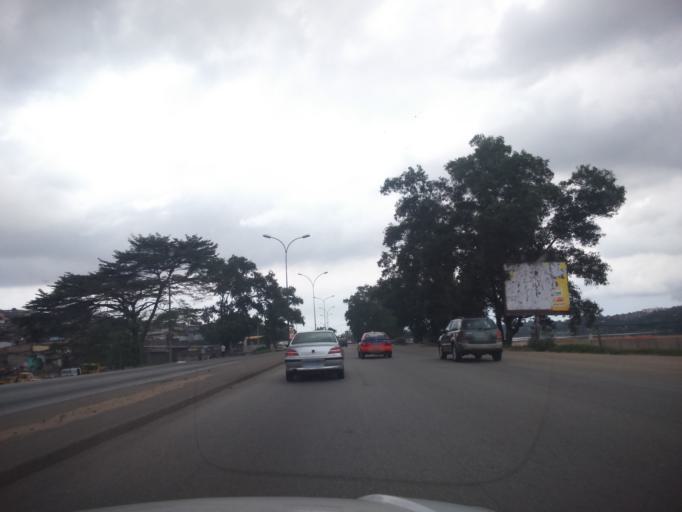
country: CI
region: Lagunes
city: Abidjan
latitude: 5.3556
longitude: -4.0402
